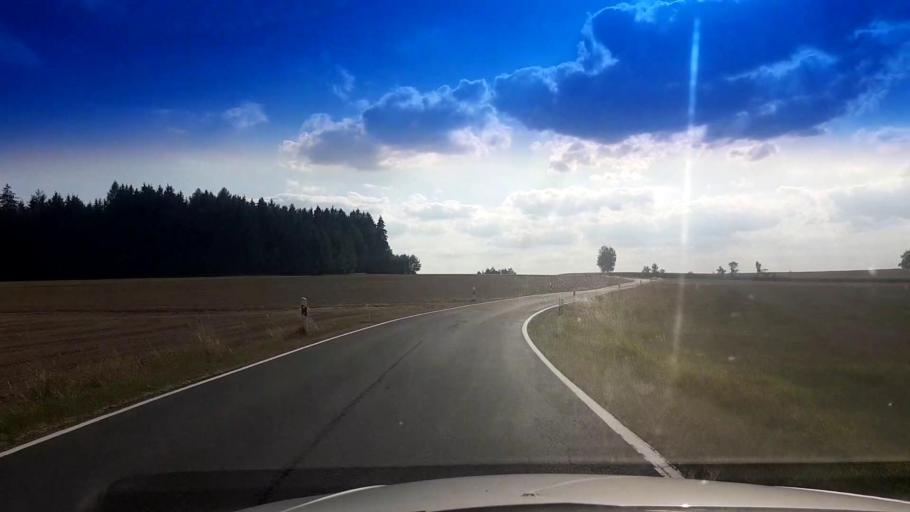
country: DE
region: Bavaria
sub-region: Upper Palatinate
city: Neualbenreuth
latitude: 49.9190
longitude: 12.4016
